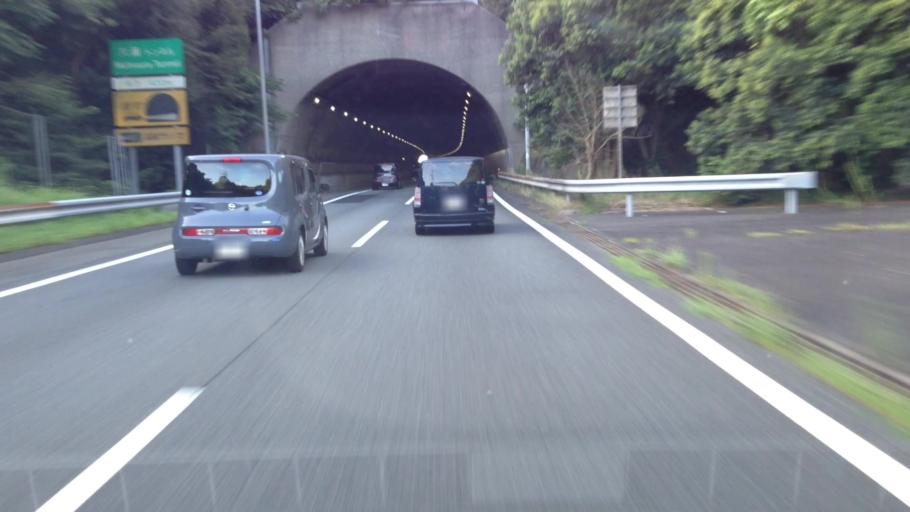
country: JP
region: Kanagawa
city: Zushi
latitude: 35.3110
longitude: 139.6072
